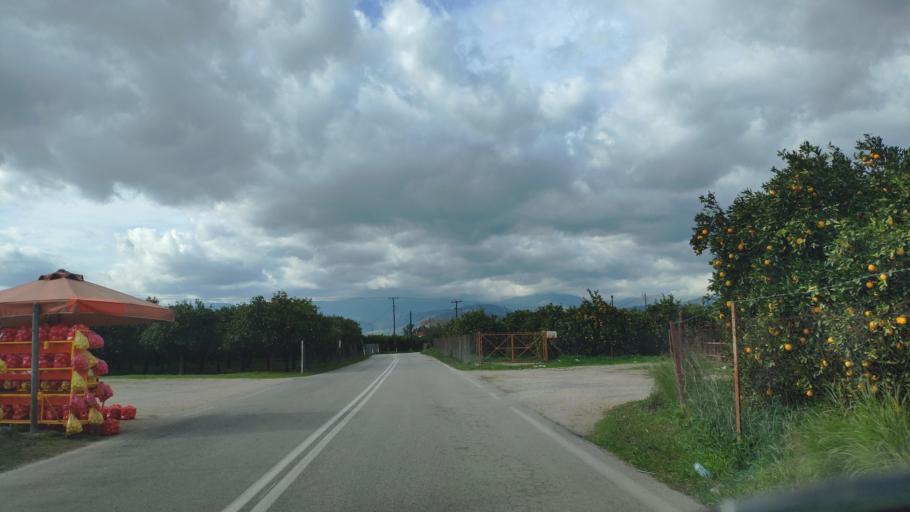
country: GR
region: Peloponnese
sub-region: Nomos Argolidos
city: Nea Tirins
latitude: 37.6085
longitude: 22.8059
